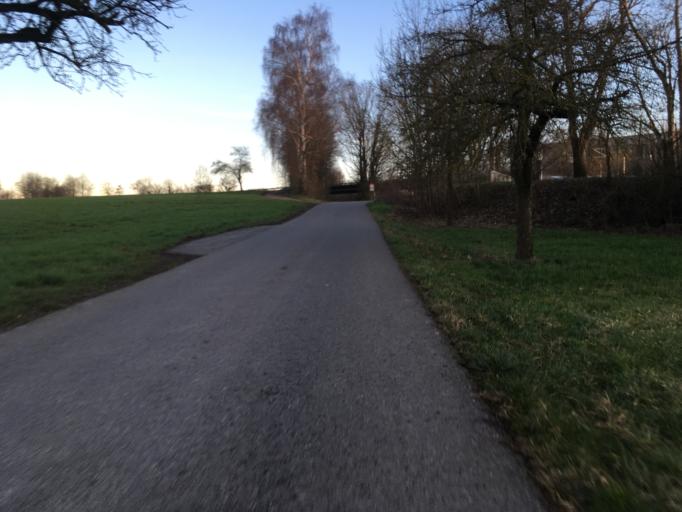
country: DE
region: Baden-Wuerttemberg
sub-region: Regierungsbezirk Stuttgart
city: Gemmingen
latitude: 49.1505
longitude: 8.9892
